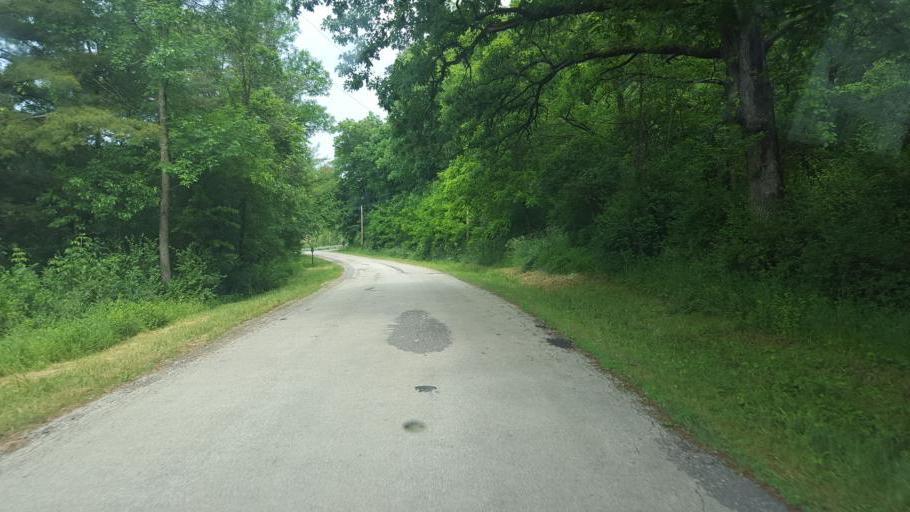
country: US
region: Wisconsin
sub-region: Monroe County
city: Cashton
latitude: 43.7112
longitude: -90.5797
